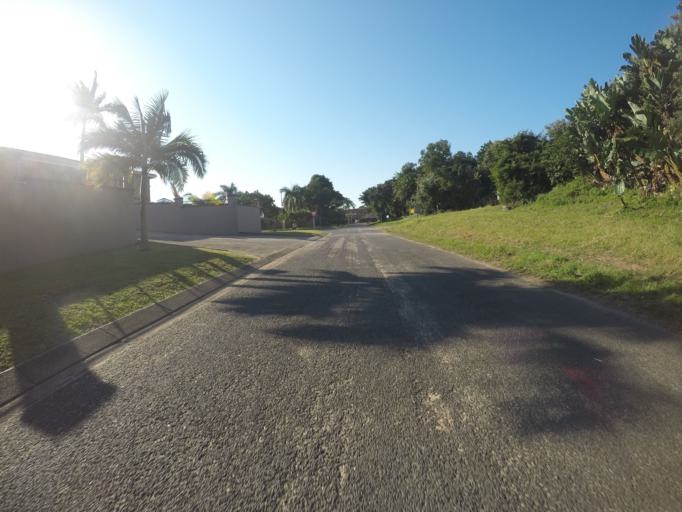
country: ZA
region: KwaZulu-Natal
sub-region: uThungulu District Municipality
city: Richards Bay
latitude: -28.7946
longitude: 32.0982
